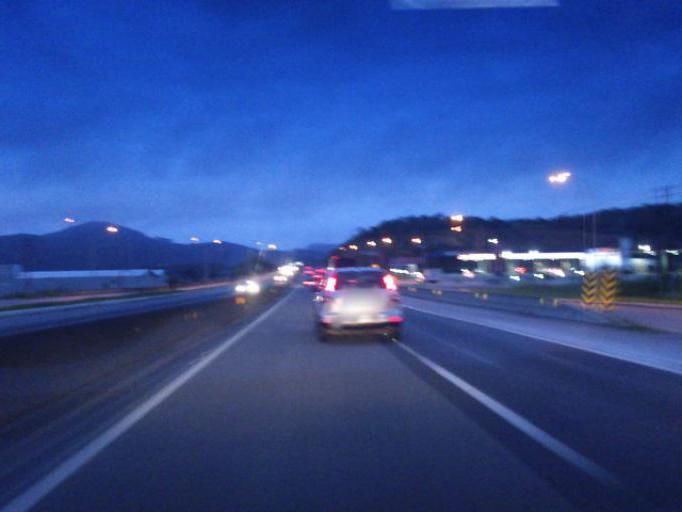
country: BR
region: Santa Catarina
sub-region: Penha
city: Penha
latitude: -26.7790
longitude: -48.6849
